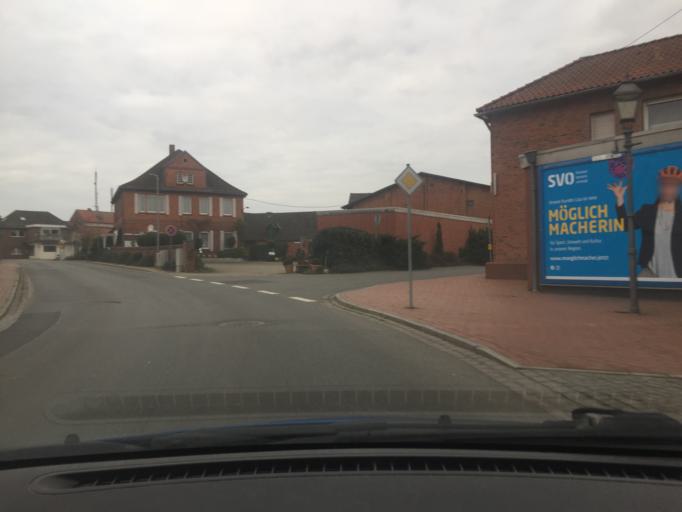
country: DE
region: Lower Saxony
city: Rosche
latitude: 52.9870
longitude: 10.7518
